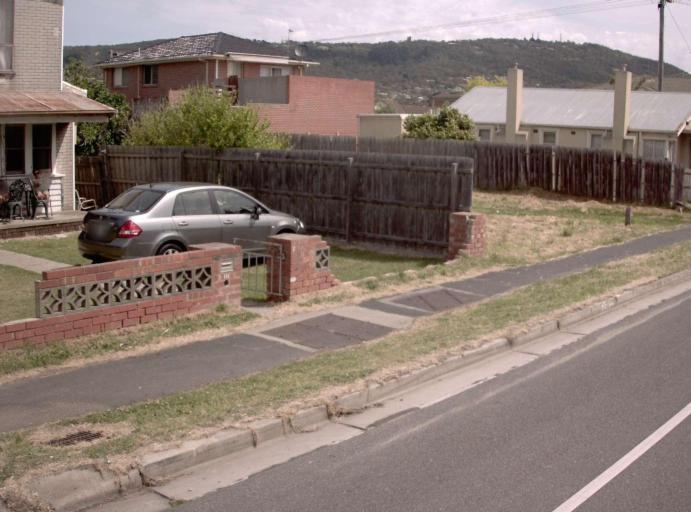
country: AU
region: Victoria
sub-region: Mornington Peninsula
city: Dromana
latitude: -38.3300
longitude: 144.9704
